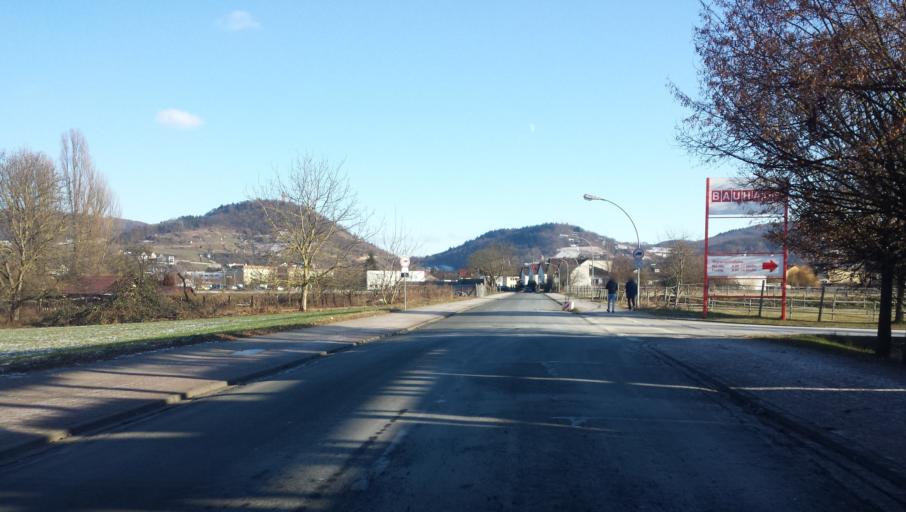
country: DE
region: Hesse
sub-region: Regierungsbezirk Darmstadt
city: Heppenheim an der Bergstrasse
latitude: 49.6422
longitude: 8.6201
